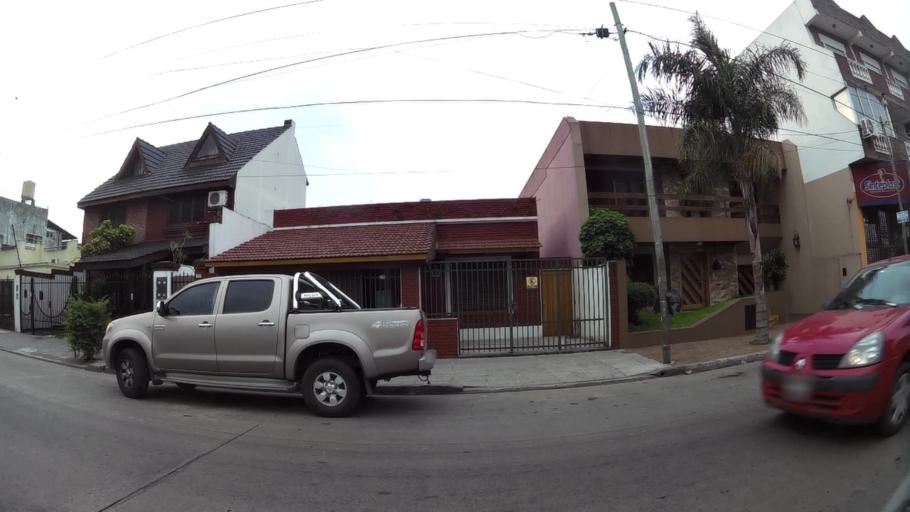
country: AR
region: Buenos Aires
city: San Justo
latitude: -34.6487
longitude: -58.5795
